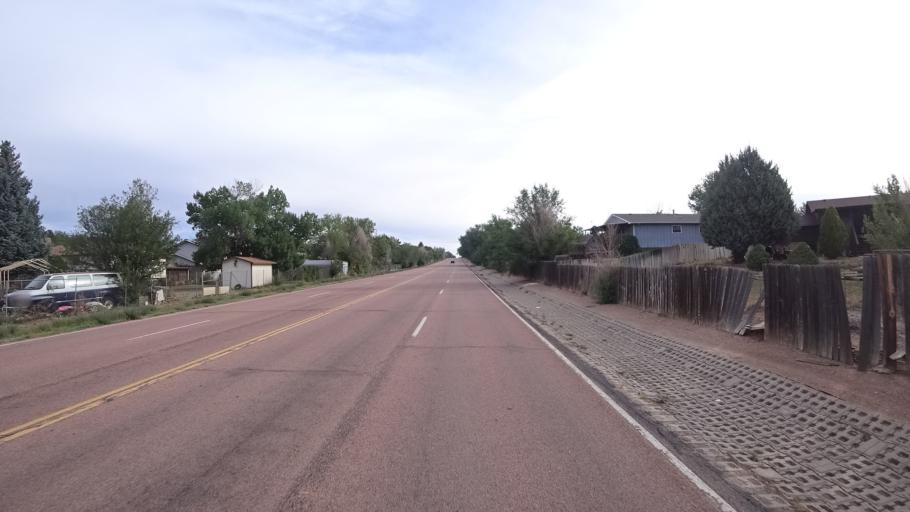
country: US
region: Colorado
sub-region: El Paso County
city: Security-Widefield
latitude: 38.7253
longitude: -104.6987
